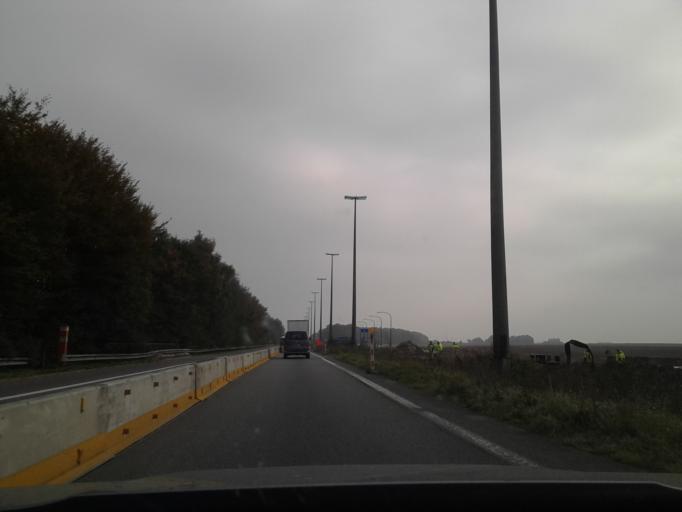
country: FR
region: Nord-Pas-de-Calais
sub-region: Departement du Nord
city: Camphin-en-Pevele
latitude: 50.6072
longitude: 3.2902
